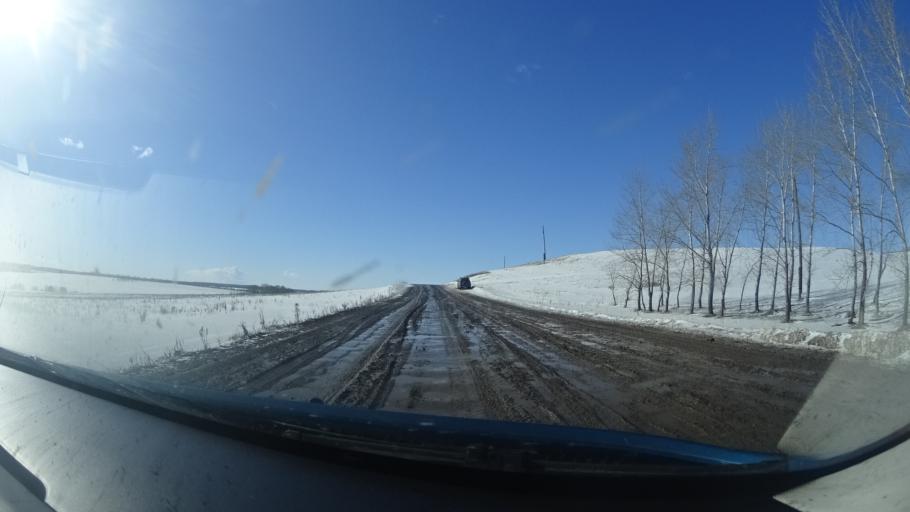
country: RU
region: Bashkortostan
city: Chishmy
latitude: 54.6021
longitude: 55.2174
